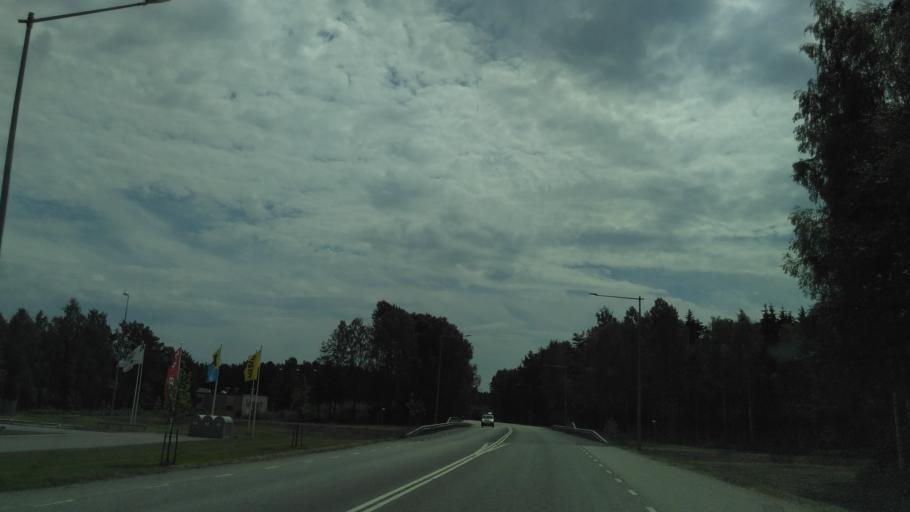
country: SE
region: Vaestra Goetaland
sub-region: Lidkopings Kommun
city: Lidkoping
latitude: 58.4928
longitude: 13.1822
